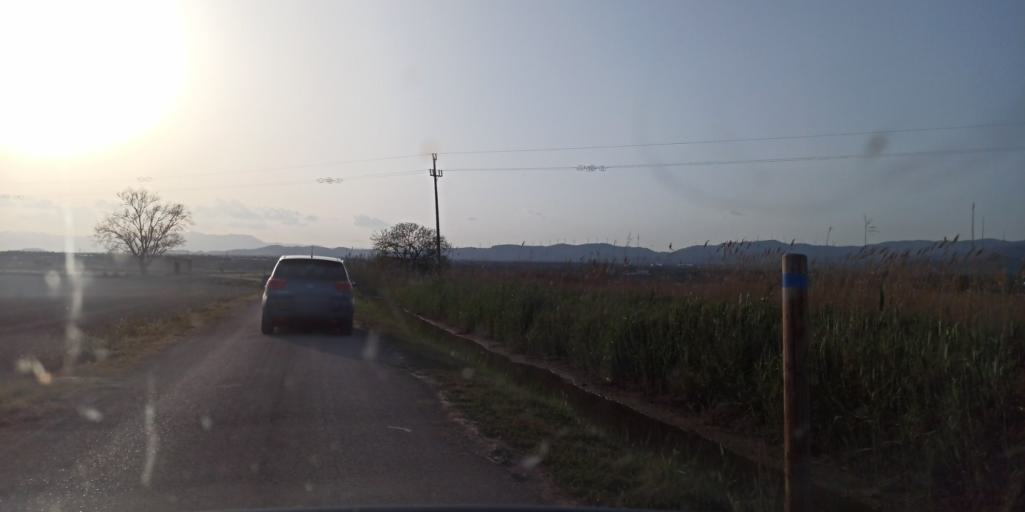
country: ES
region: Catalonia
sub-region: Provincia de Tarragona
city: L'Ampolla
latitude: 40.7850
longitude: 0.6983
